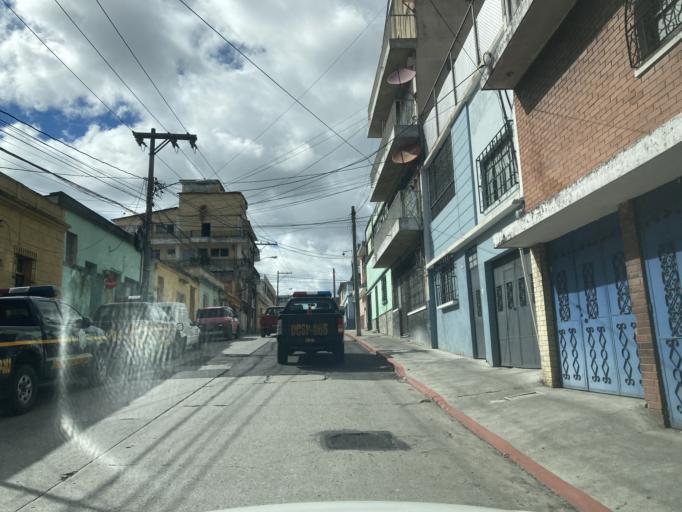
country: GT
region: Guatemala
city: Guatemala City
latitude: 14.6462
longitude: -90.5090
